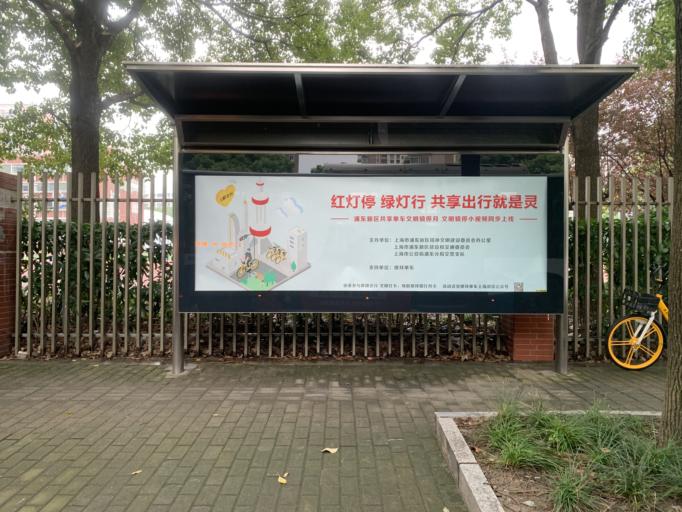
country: CN
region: Shanghai Shi
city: Huamu
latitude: 31.2271
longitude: 121.5533
